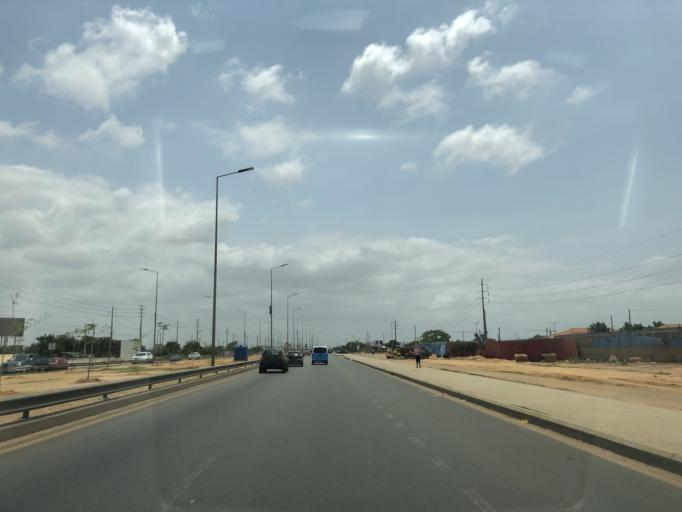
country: AO
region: Luanda
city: Luanda
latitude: -8.9441
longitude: 13.2605
